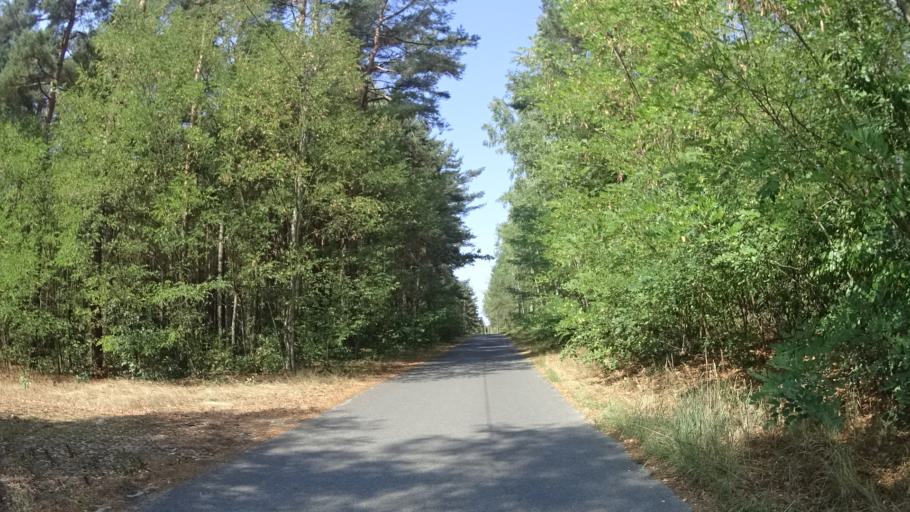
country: DE
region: Brandenburg
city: Tschernitz
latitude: 51.5995
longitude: 14.5904
